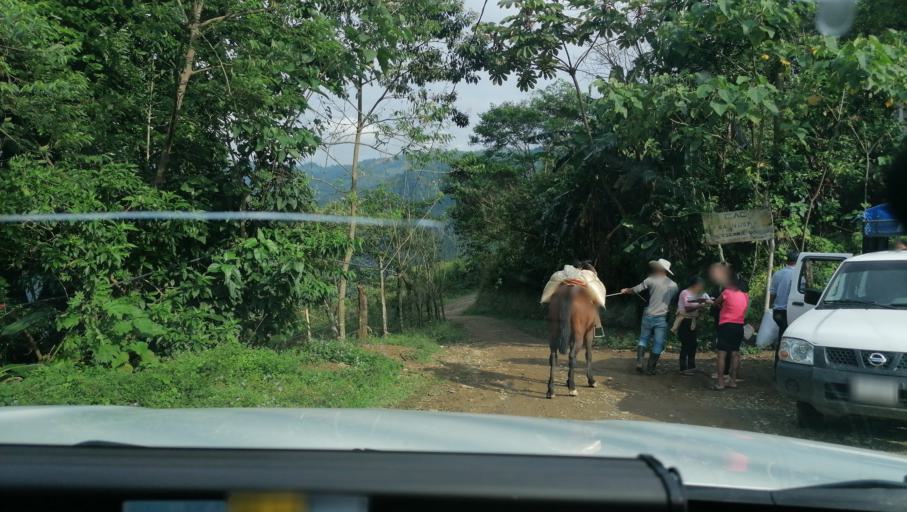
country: MX
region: Chiapas
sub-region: Tapilula
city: San Francisco Jacona
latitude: 17.3148
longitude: -93.1016
